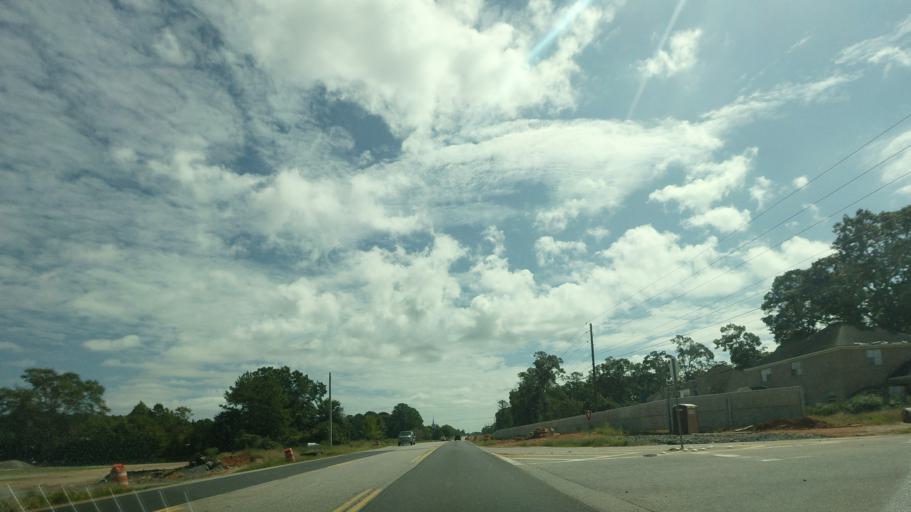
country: US
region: Georgia
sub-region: Houston County
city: Warner Robins
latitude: 32.5545
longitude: -83.6428
